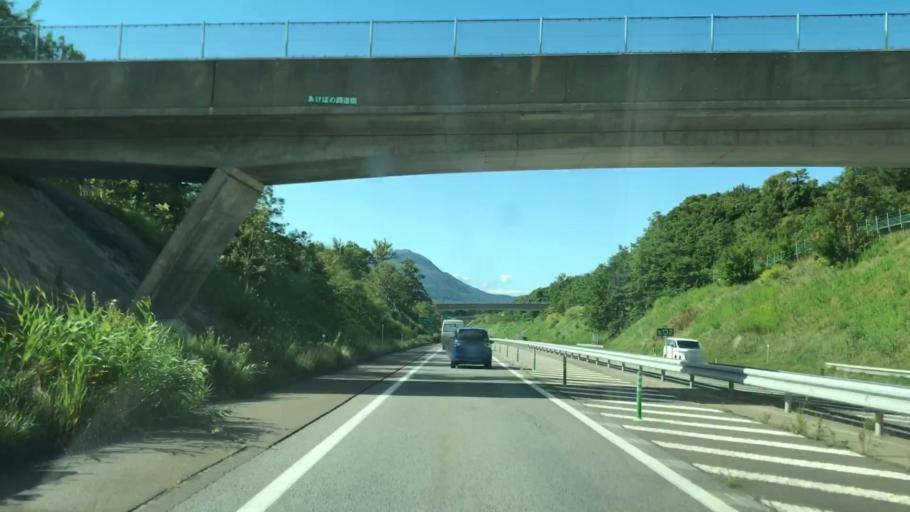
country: JP
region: Hokkaido
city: Date
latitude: 42.4764
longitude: 140.9019
